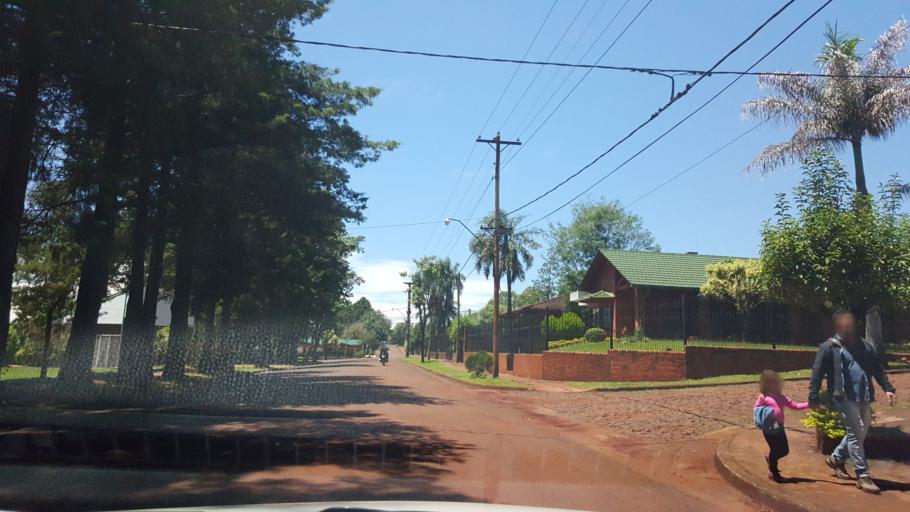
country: AR
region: Misiones
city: Capiovi
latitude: -26.9321
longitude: -55.0589
